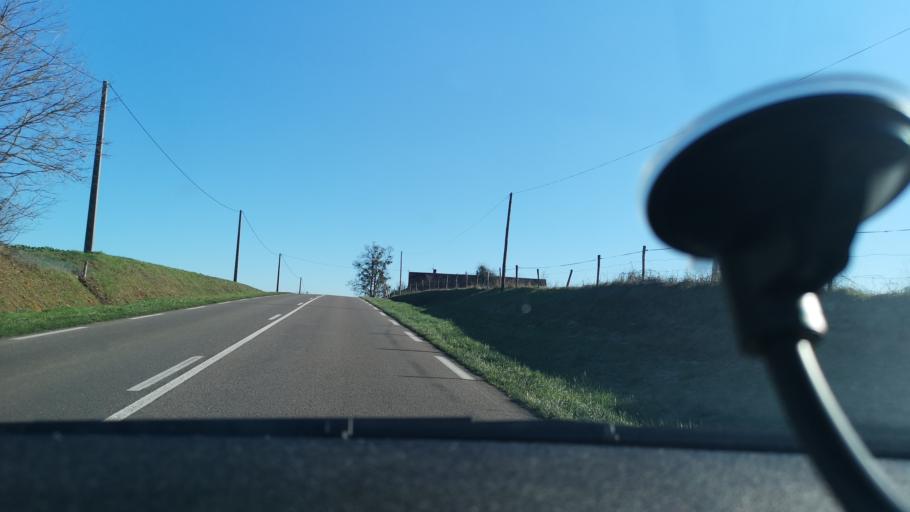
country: FR
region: Bourgogne
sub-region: Departement de Saone-et-Loire
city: Saint-Germain-du-Plain
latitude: 46.7515
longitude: 5.0321
